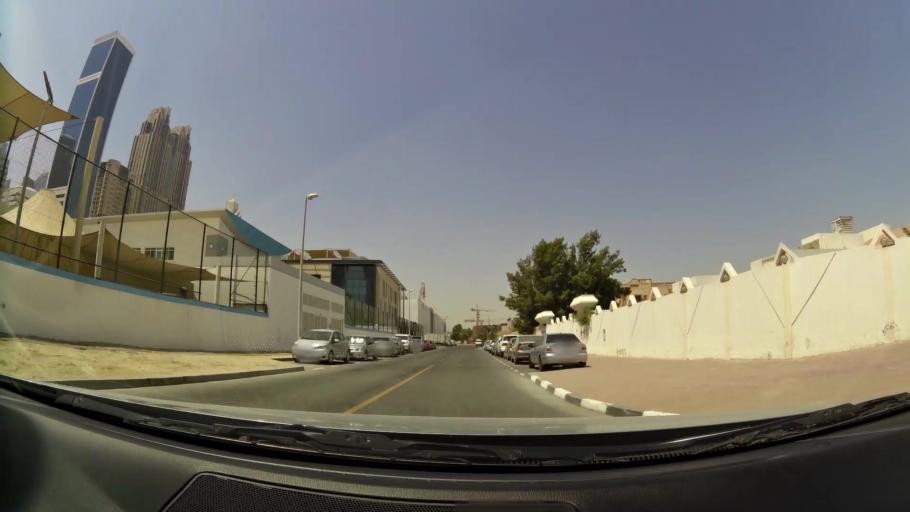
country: AE
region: Dubai
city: Dubai
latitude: 25.2118
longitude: 55.2713
